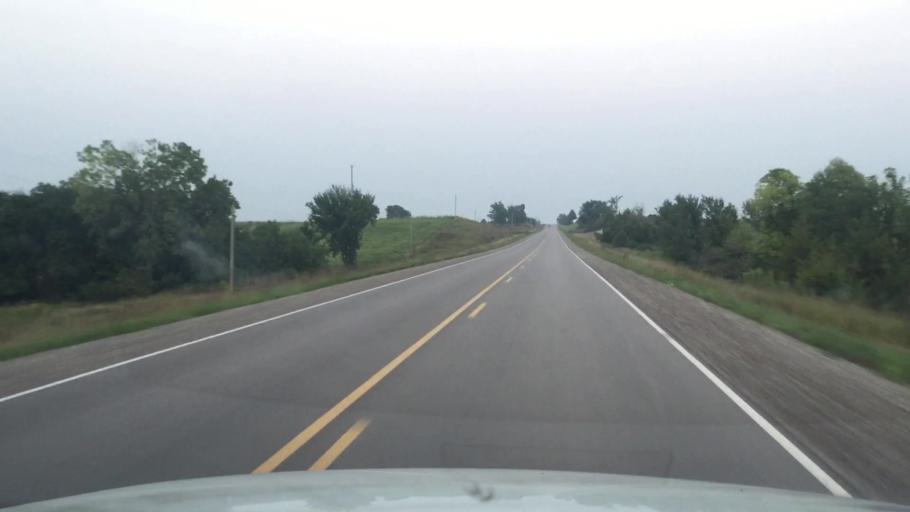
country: US
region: Iowa
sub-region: Marion County
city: Melcher-Dallas
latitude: 41.1895
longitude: -93.4151
